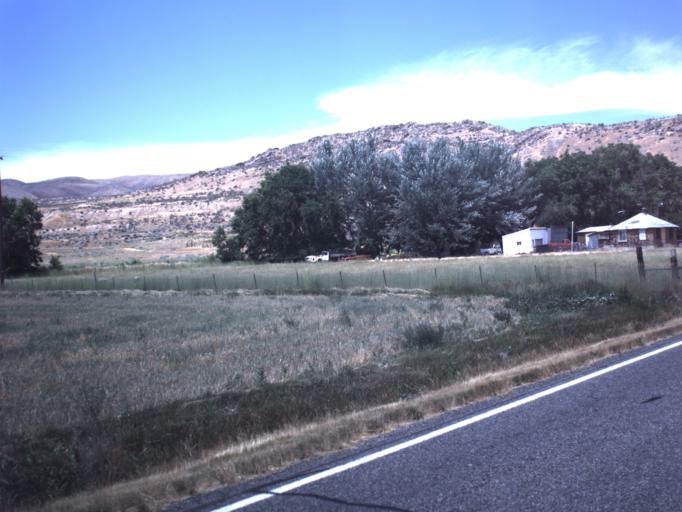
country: US
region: Utah
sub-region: Box Elder County
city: Tremonton
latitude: 41.6332
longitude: -112.3308
